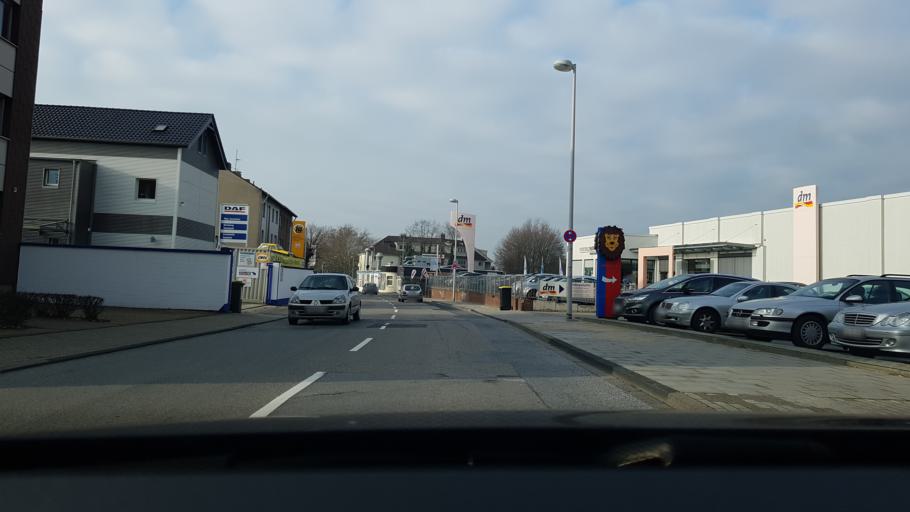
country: DE
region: North Rhine-Westphalia
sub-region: Regierungsbezirk Dusseldorf
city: Muelheim (Ruhr)
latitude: 51.4355
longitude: 6.9204
